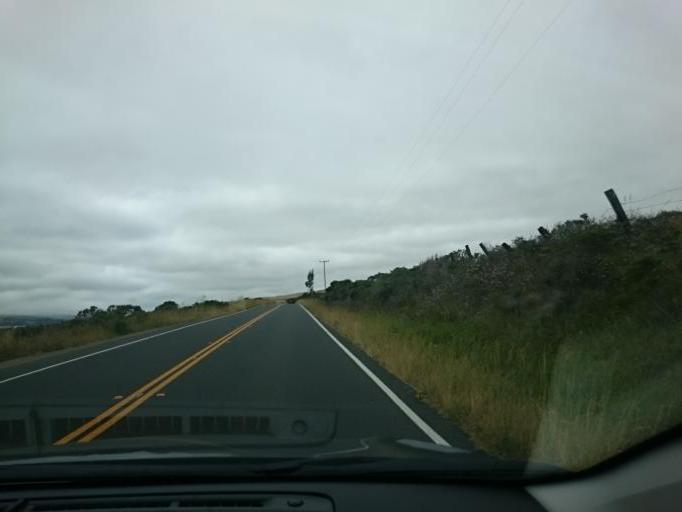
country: US
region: California
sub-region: Marin County
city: Inverness
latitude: 38.1216
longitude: -122.8560
